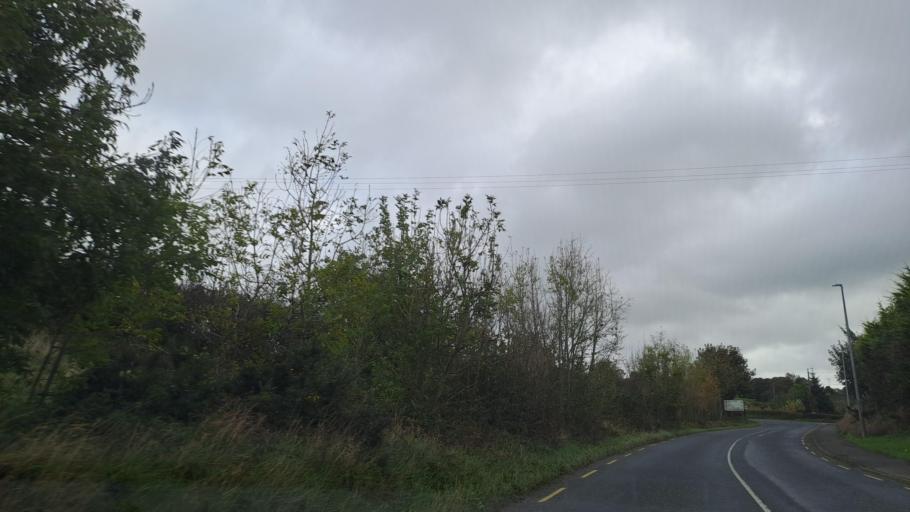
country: IE
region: Ulster
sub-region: An Cabhan
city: Bailieborough
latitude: 53.9190
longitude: -6.9582
